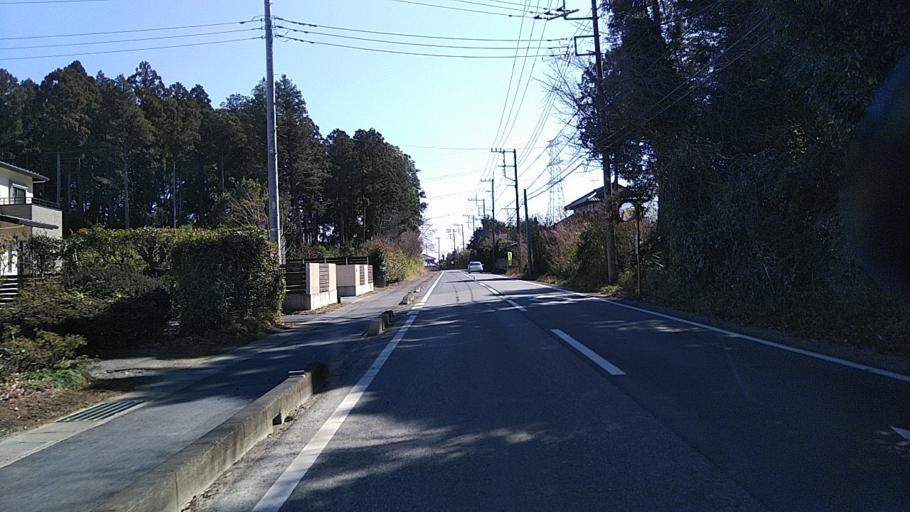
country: JP
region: Ibaraki
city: Ishige
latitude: 36.0851
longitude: 140.0299
